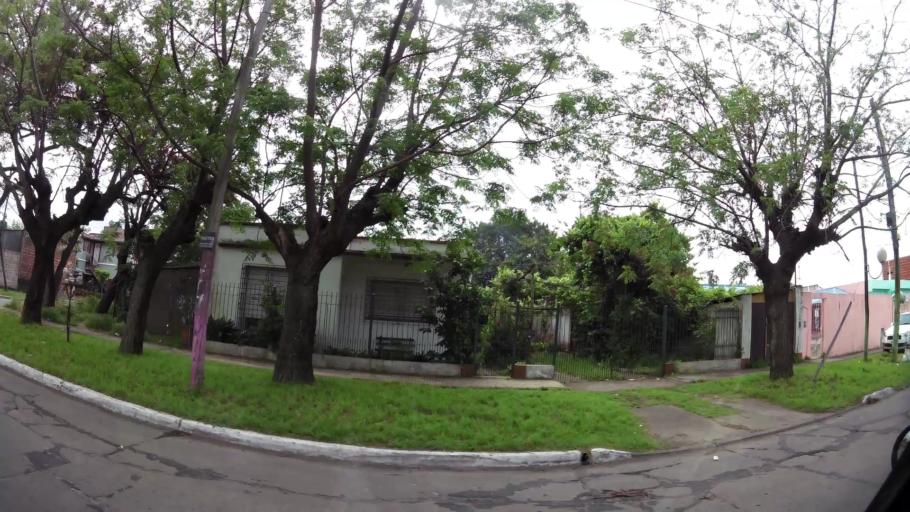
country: AR
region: Buenos Aires
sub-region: Partido de Quilmes
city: Quilmes
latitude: -34.7621
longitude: -58.2692
